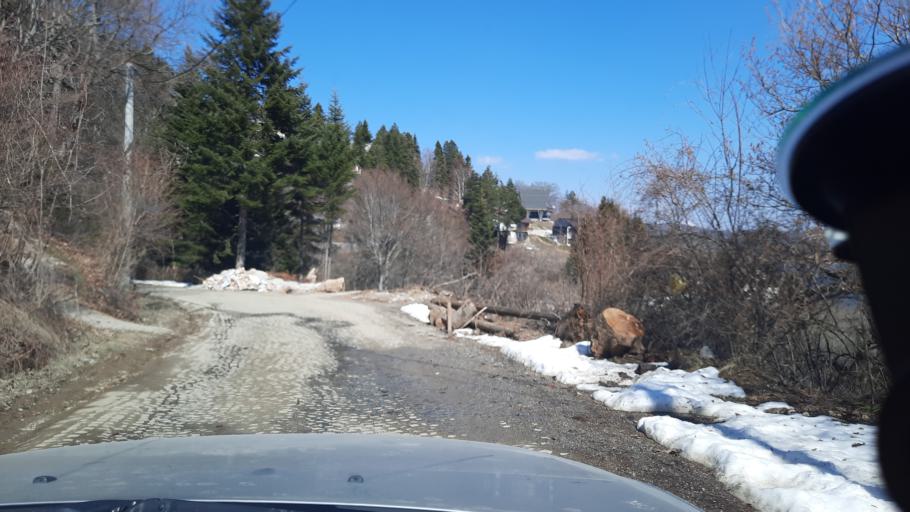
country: MK
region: Gostivar
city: Vrutok
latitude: 41.7026
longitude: 20.7575
